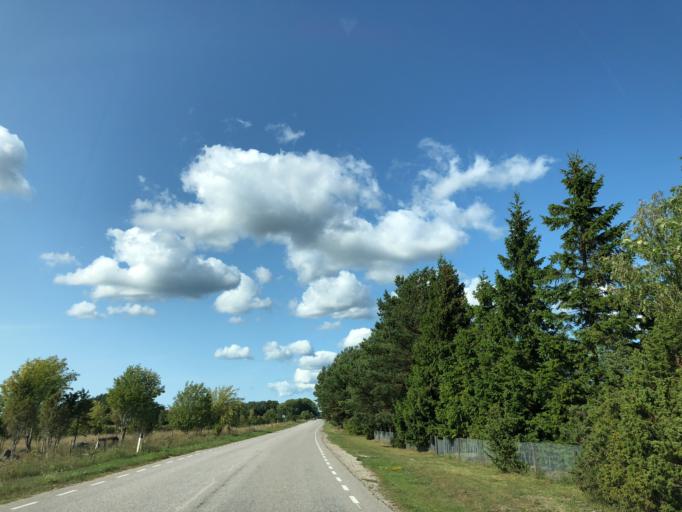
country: EE
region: Hiiumaa
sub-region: Kaerdla linn
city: Kardla
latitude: 58.7911
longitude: 22.7704
